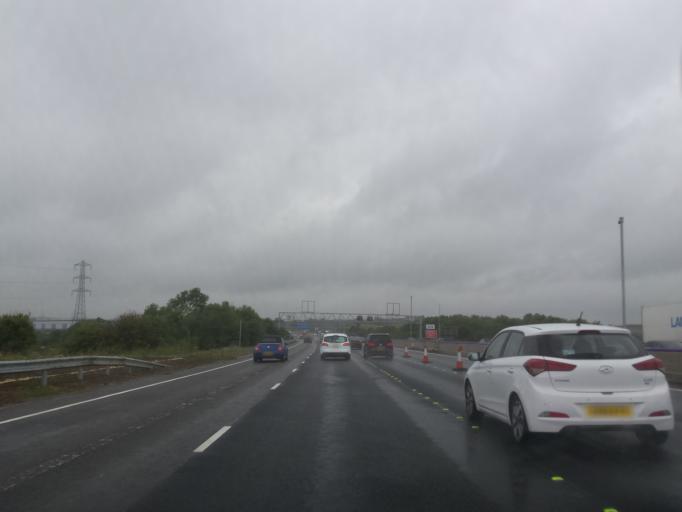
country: GB
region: England
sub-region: Derbyshire
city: Staveley
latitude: 53.2555
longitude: -1.3221
